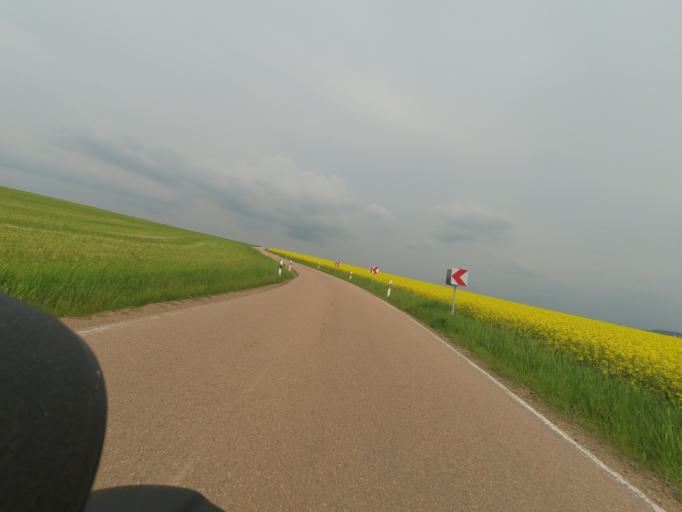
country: DE
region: Saxony
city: Pretzschendorf
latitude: 50.8732
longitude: 13.5357
